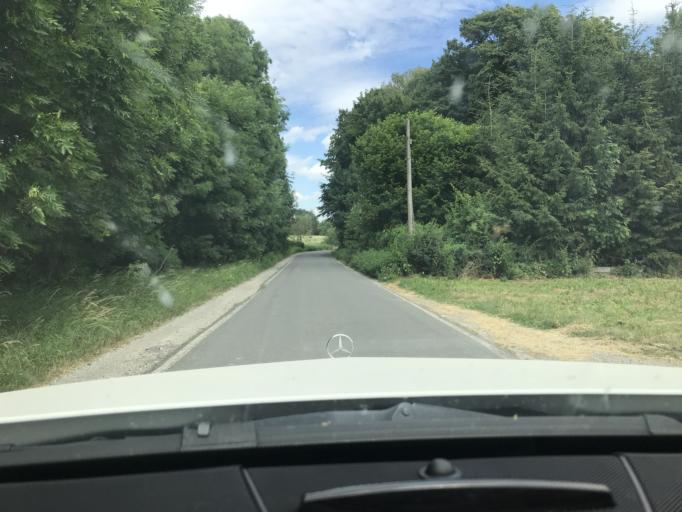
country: DE
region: Thuringia
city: Holzsussra
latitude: 51.2968
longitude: 10.6482
